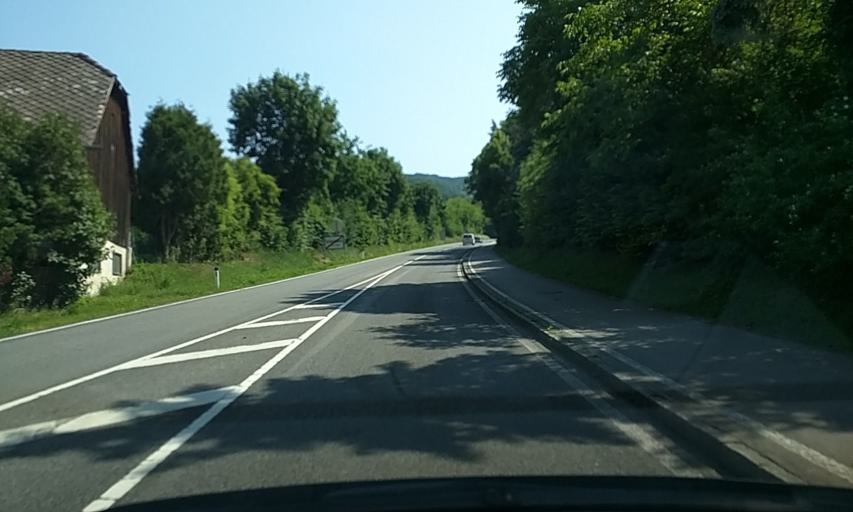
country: AT
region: Lower Austria
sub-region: Politischer Bezirk Melk
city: Emmersdorf an der Donau
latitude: 48.2563
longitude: 15.3739
